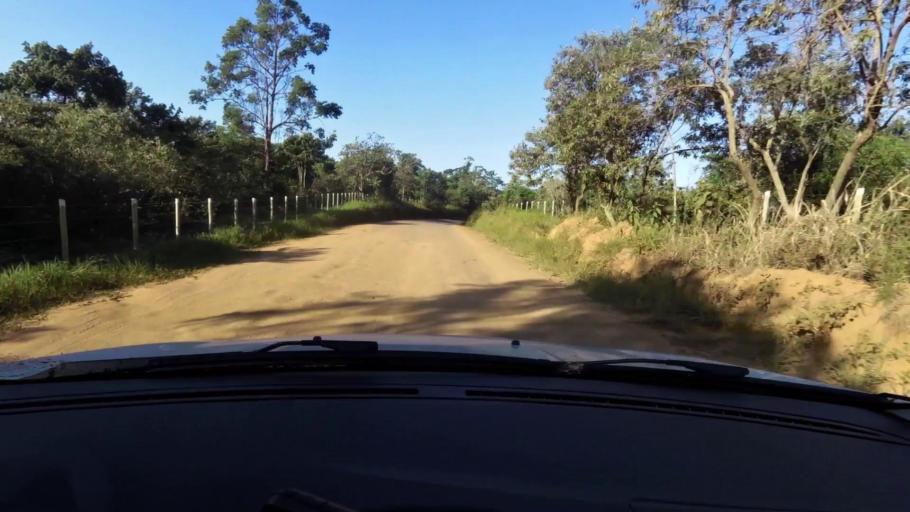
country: BR
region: Espirito Santo
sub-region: Guarapari
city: Guarapari
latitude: -20.7324
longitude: -40.5938
